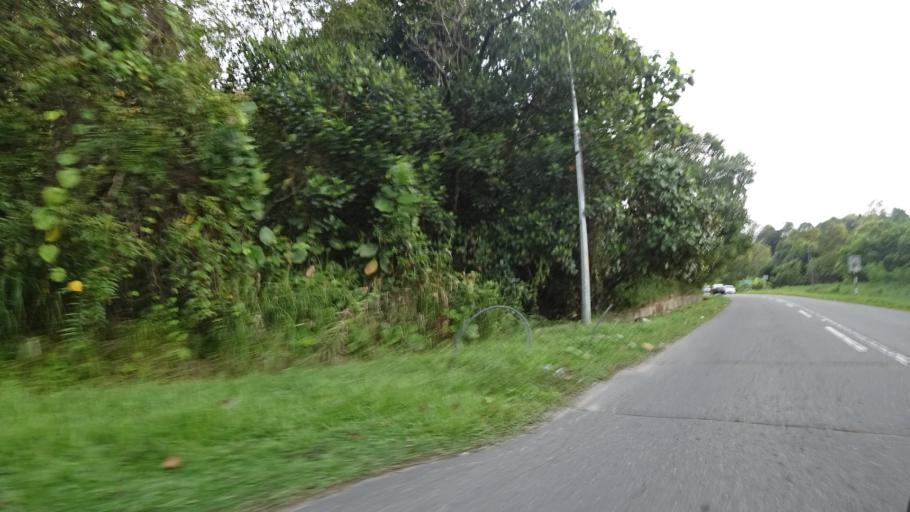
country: BN
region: Brunei and Muara
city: Bandar Seri Begawan
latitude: 4.8538
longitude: 114.8216
